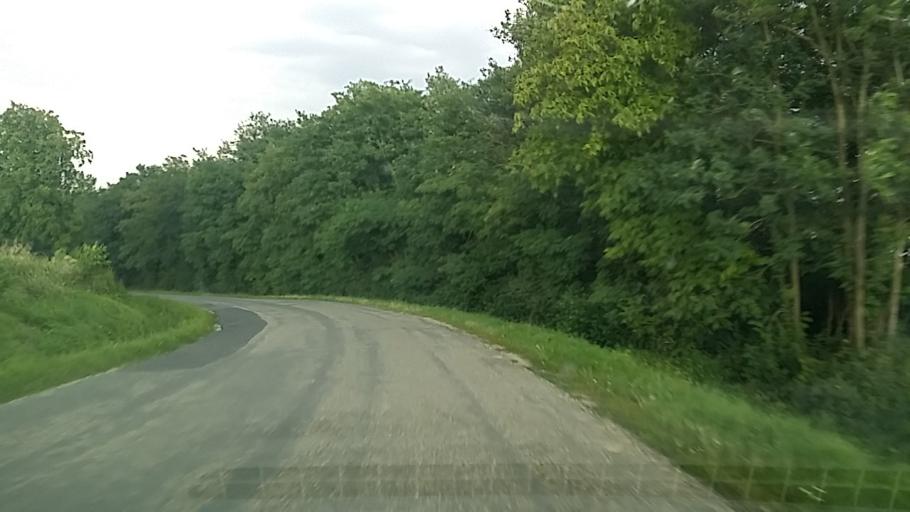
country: HU
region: Zala
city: Nagykanizsa
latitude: 46.4977
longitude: 17.0729
